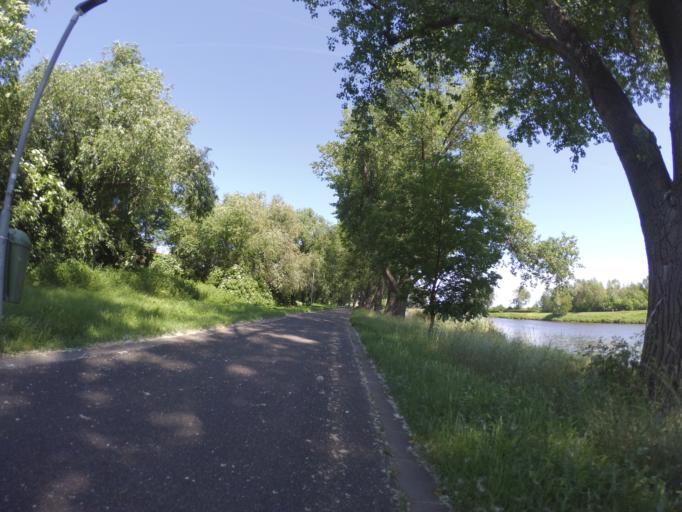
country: CZ
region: Central Bohemia
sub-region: Okres Nymburk
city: Nymburk
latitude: 50.1774
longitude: 15.0249
